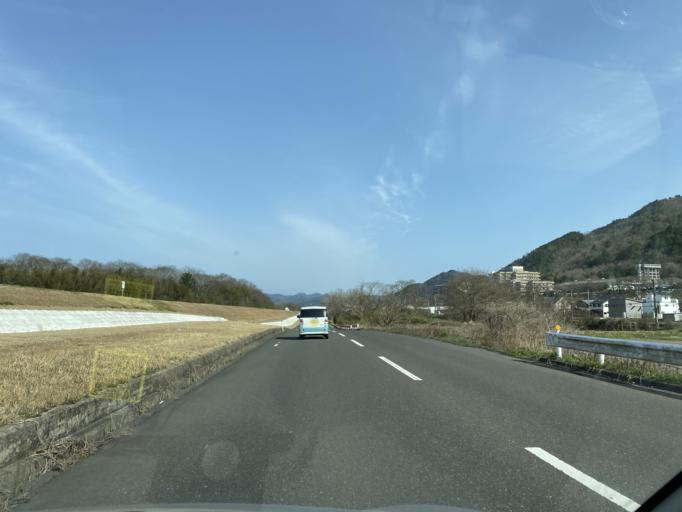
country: JP
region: Kyoto
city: Ayabe
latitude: 35.3064
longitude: 135.2120
